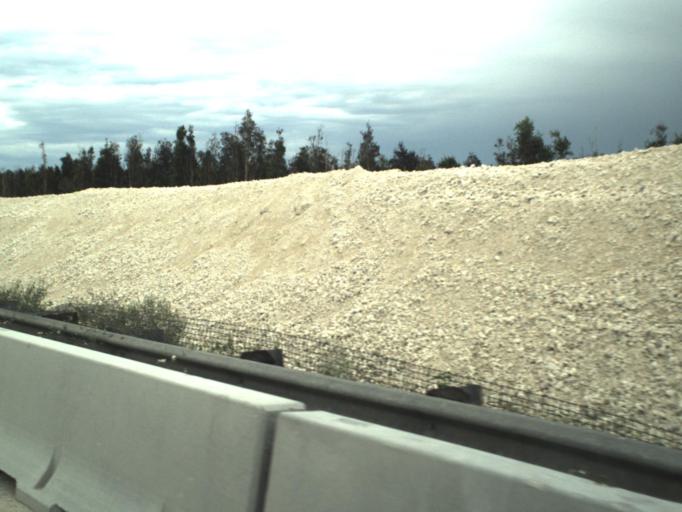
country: US
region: Florida
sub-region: Miami-Dade County
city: Kendall West
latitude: 25.7460
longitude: -80.4808
